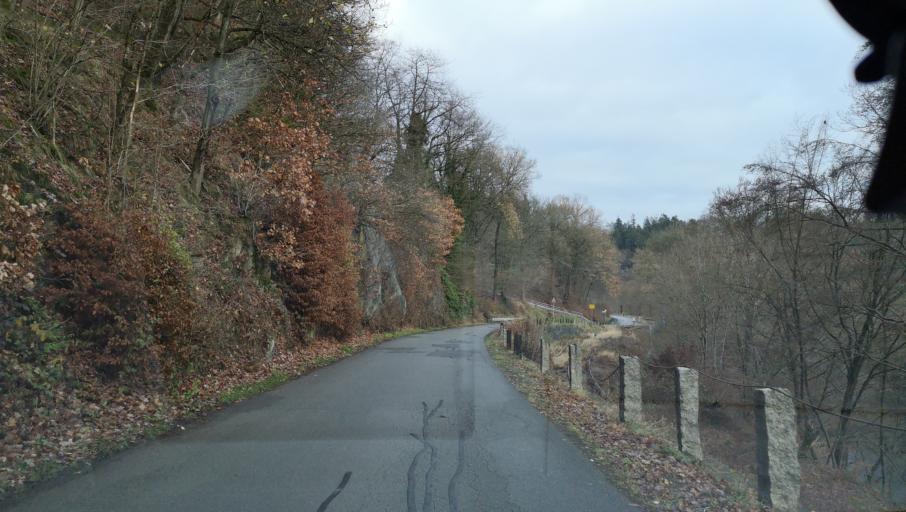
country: DE
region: North Rhine-Westphalia
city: Radevormwald
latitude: 51.2032
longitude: 7.3008
